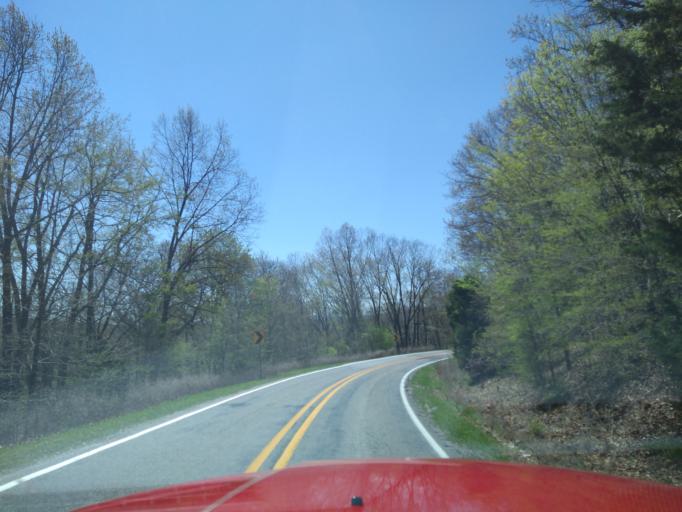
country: US
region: Arkansas
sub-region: Washington County
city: West Fork
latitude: 35.7875
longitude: -94.2547
